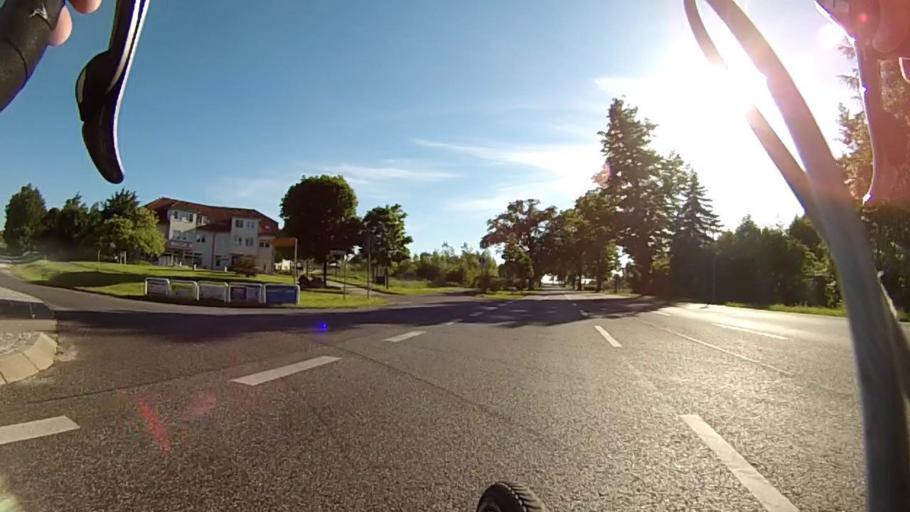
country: DE
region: Brandenburg
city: Werneuchen
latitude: 52.6220
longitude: 13.6745
